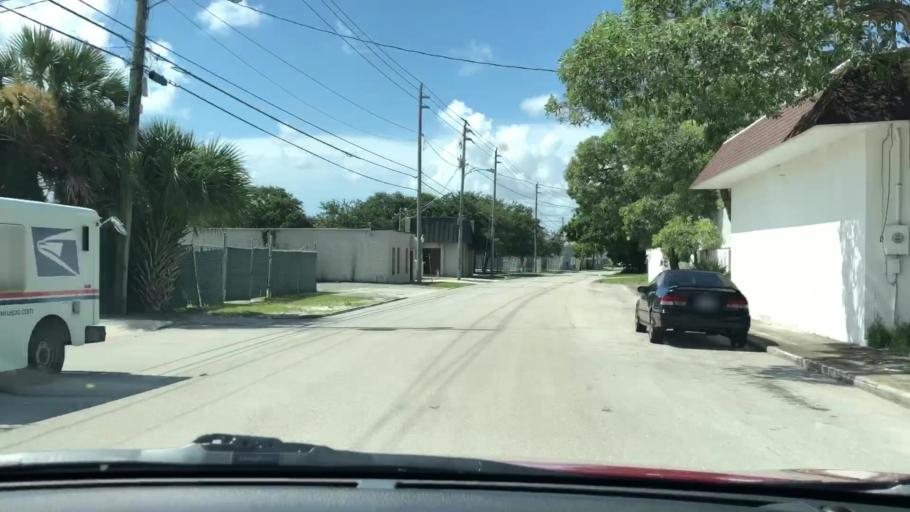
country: US
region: Florida
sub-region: Palm Beach County
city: West Palm Beach
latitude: 26.7012
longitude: -80.0635
